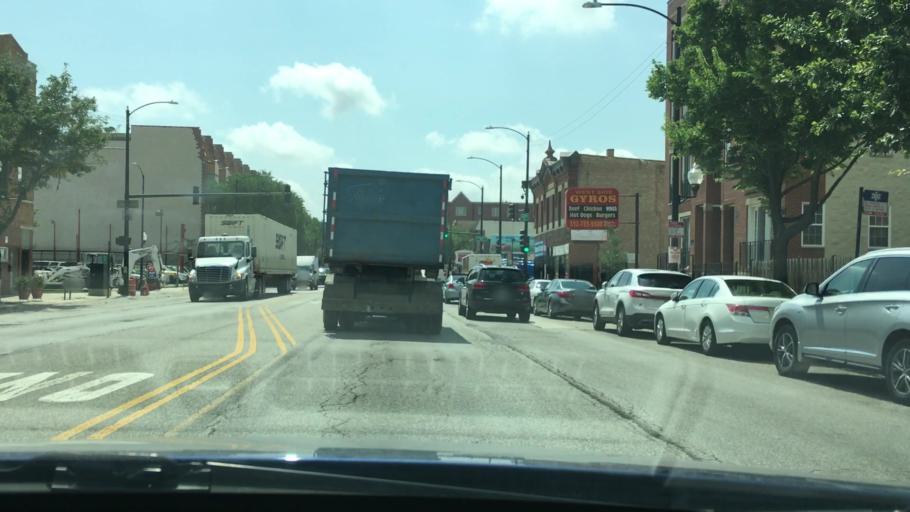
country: US
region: Illinois
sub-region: Cook County
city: Chicago
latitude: 41.8719
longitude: -87.6862
